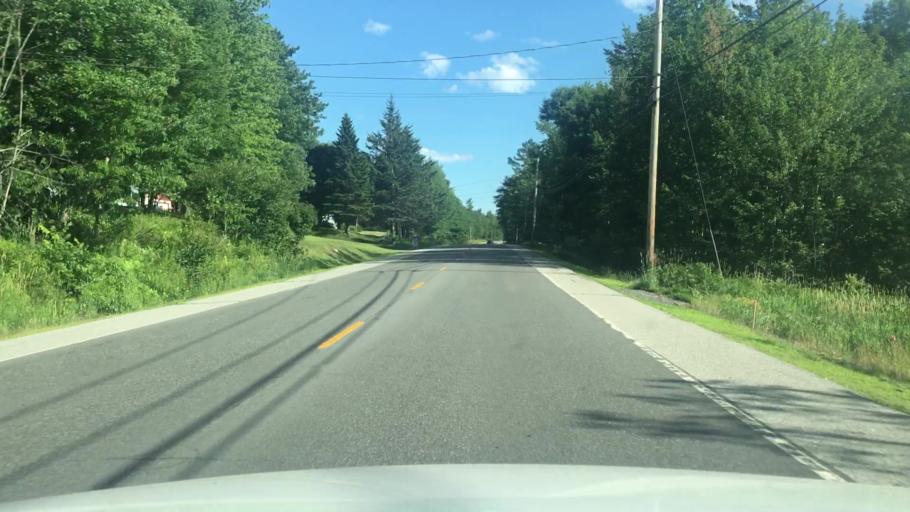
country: US
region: Maine
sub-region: Franklin County
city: Jay
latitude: 44.5432
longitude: -70.2364
